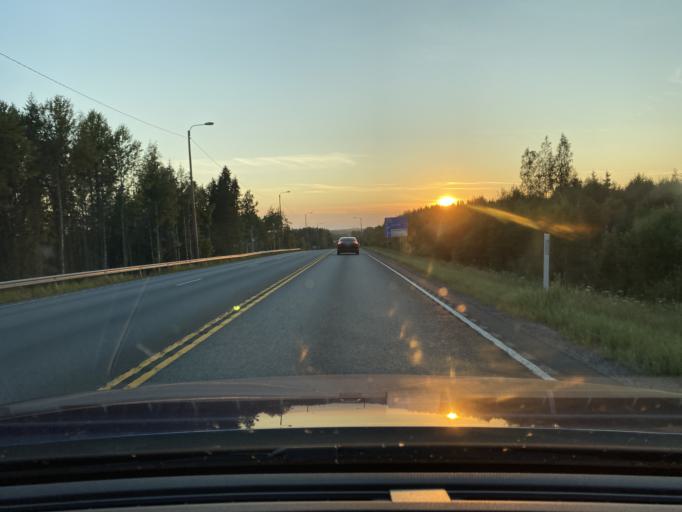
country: FI
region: Pirkanmaa
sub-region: Luoteis-Pirkanmaa
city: Ikaalinen
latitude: 61.7486
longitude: 23.0868
